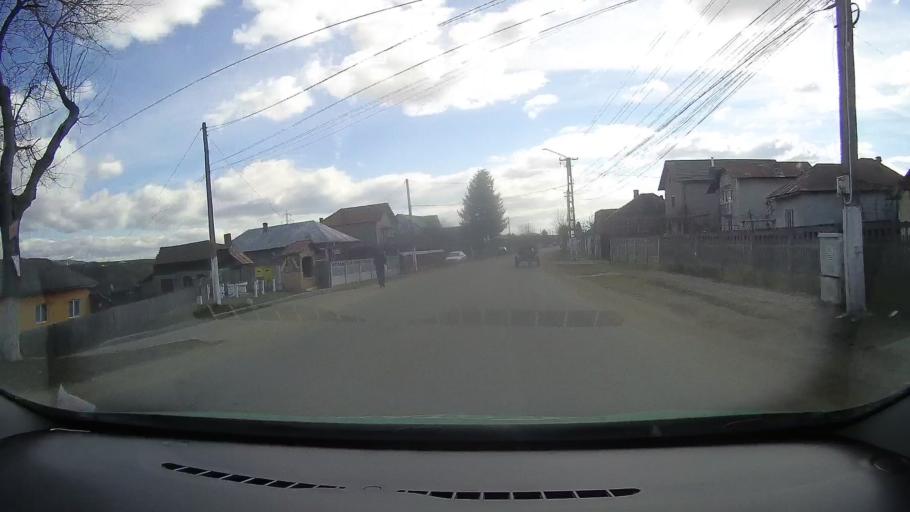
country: RO
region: Dambovita
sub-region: Comuna Doicesti
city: Doicesti
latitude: 44.9847
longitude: 25.3865
